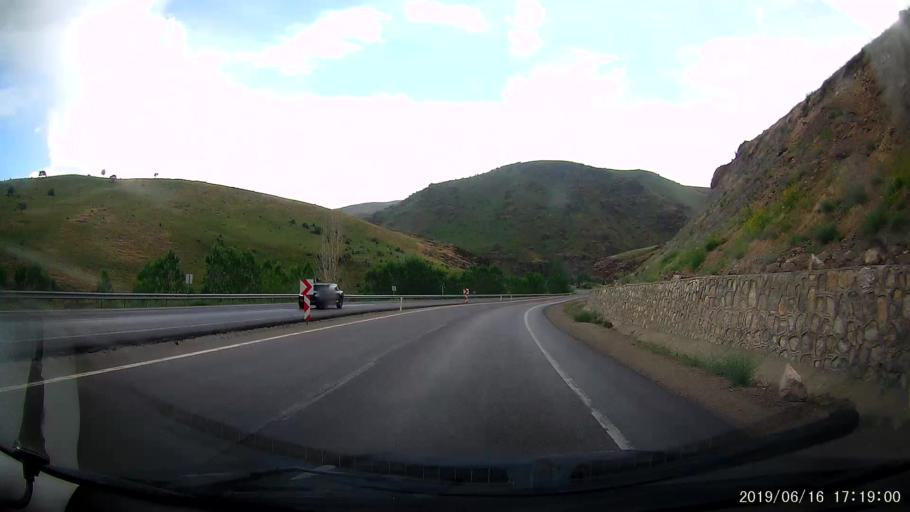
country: TR
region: Erzincan
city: Tercan
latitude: 39.8062
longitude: 40.5316
